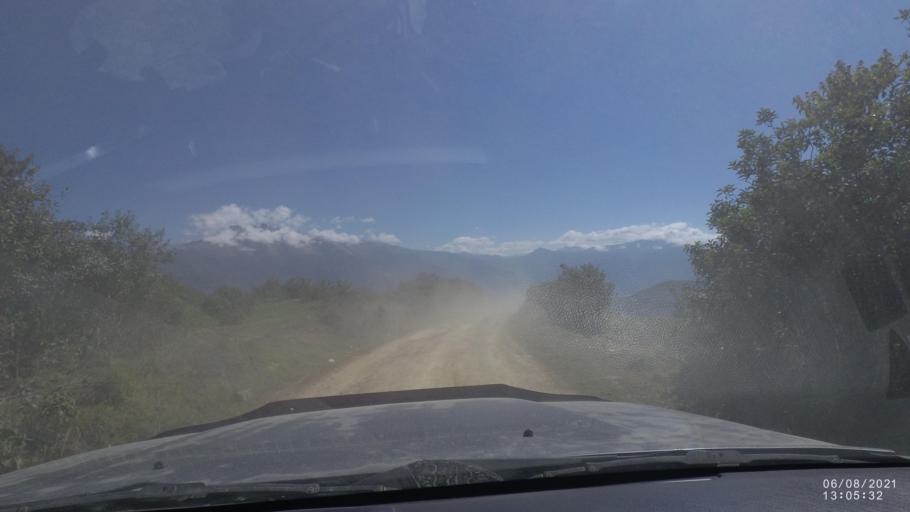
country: BO
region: La Paz
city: Quime
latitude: -16.7342
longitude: -66.7031
